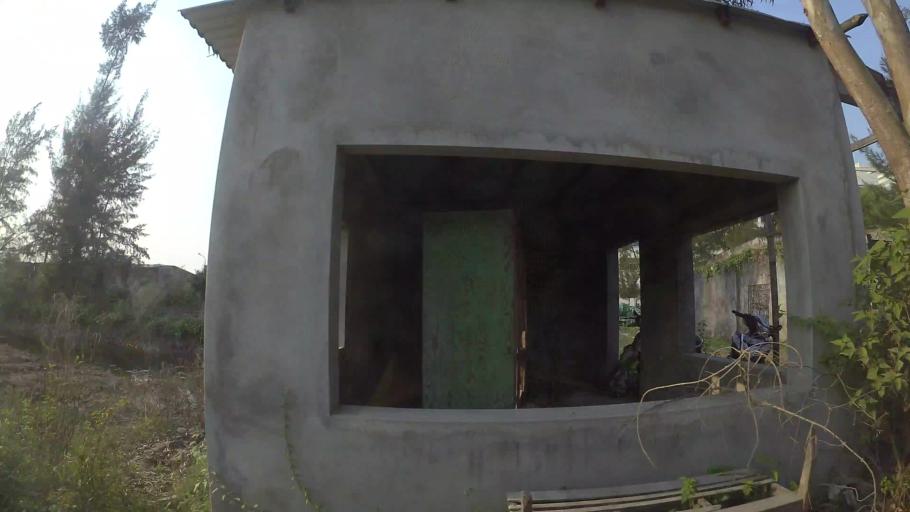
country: VN
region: Da Nang
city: Ngu Hanh Son
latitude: 15.9714
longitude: 108.2491
